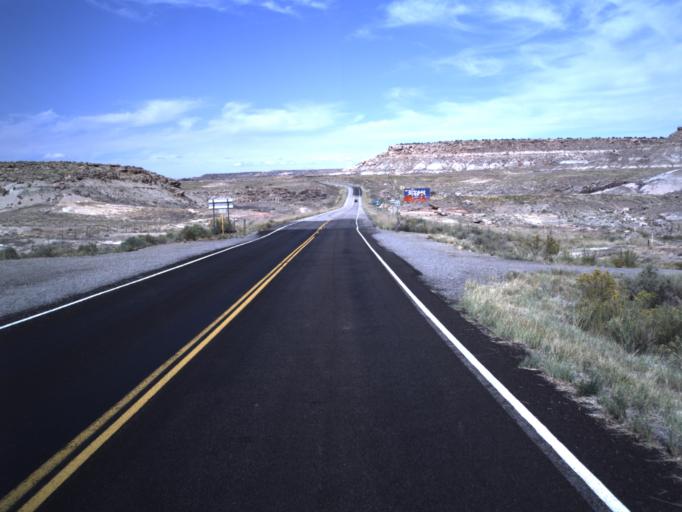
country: US
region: Colorado
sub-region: Montezuma County
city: Towaoc
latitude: 37.1494
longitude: -109.0447
